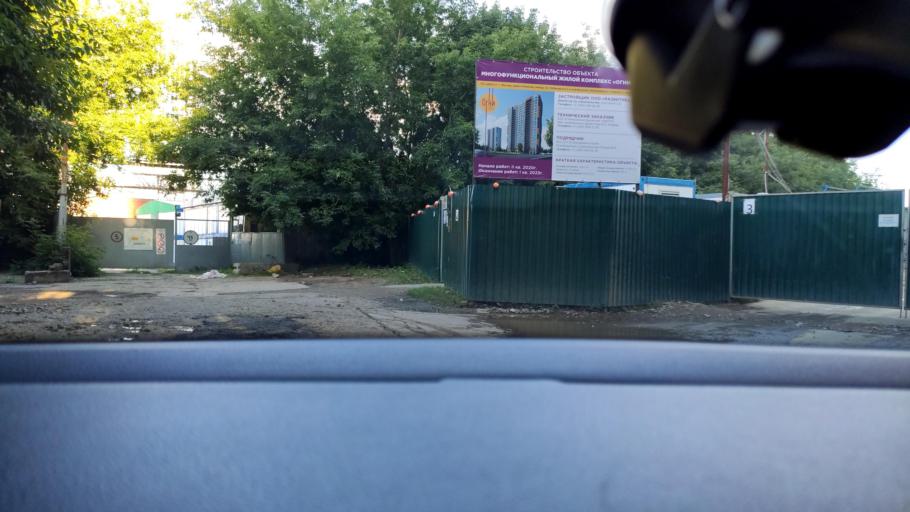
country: RU
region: Moscow
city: Amin'yevo
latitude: 55.6988
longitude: 37.4754
